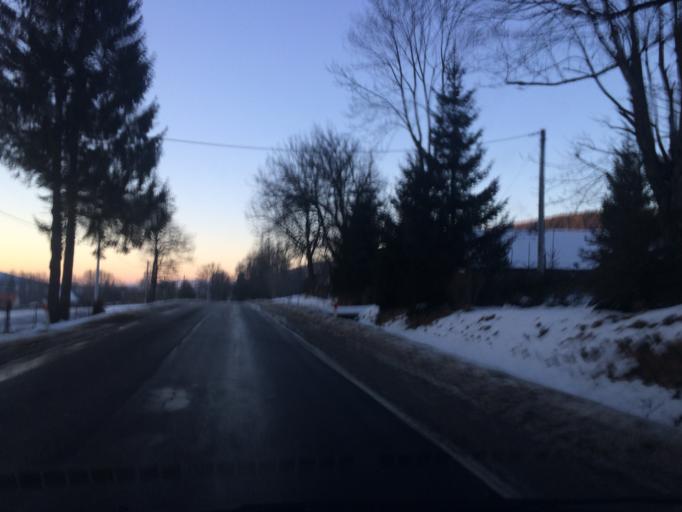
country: PL
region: Subcarpathian Voivodeship
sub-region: Powiat bieszczadzki
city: Czarna
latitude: 49.3555
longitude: 22.6789
